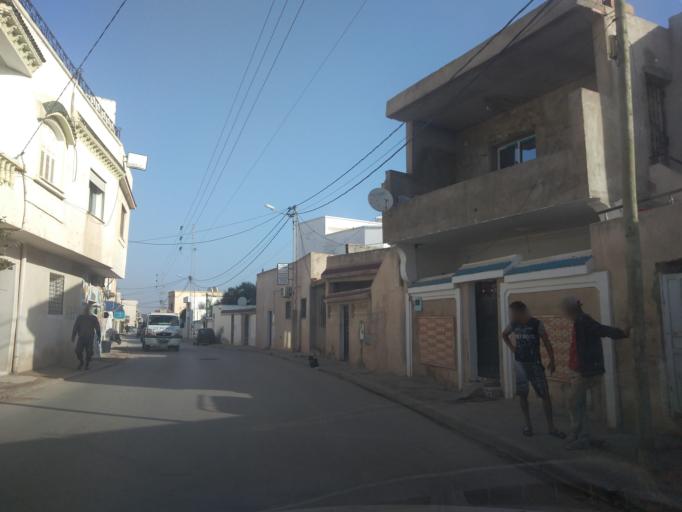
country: TN
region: Manouba
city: Manouba
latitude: 36.7929
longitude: 10.0890
